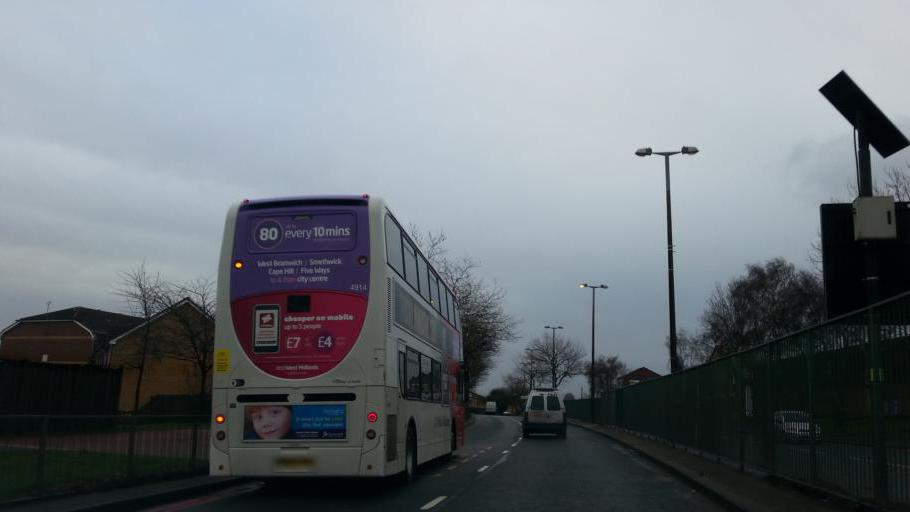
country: GB
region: England
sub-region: Sandwell
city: West Bromwich
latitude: 52.5025
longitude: -1.9893
